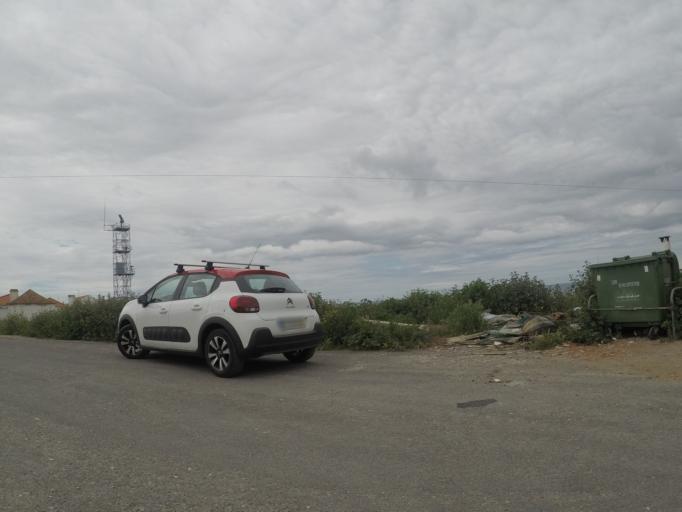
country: PT
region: Beja
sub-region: Odemira
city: Sao Teotonio
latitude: 37.5501
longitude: -8.7922
